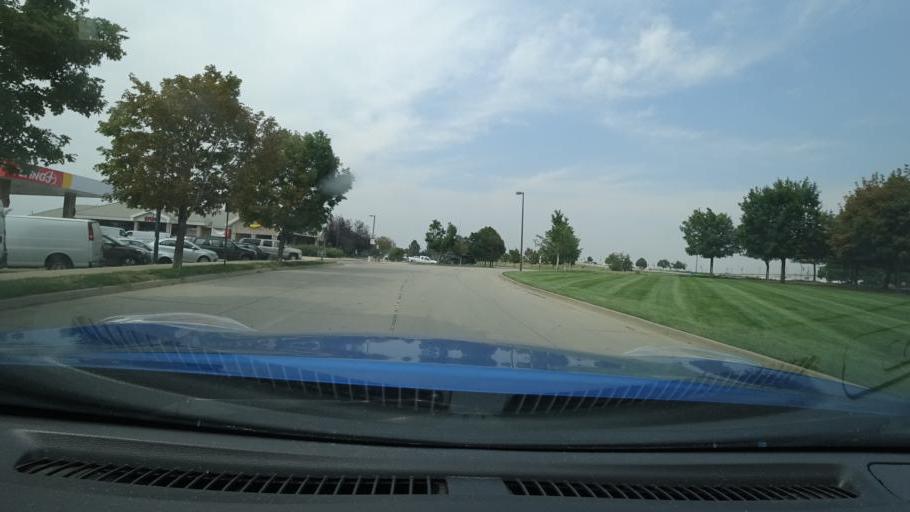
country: US
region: Colorado
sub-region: Adams County
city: Aurora
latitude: 39.7622
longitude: -104.7924
